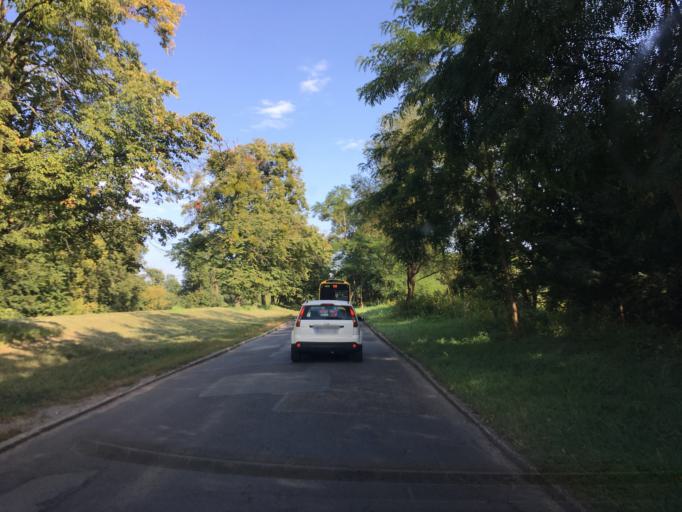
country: PL
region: Lower Silesian Voivodeship
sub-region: Powiat wroclawski
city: Radwanice
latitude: 51.0934
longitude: 17.0861
